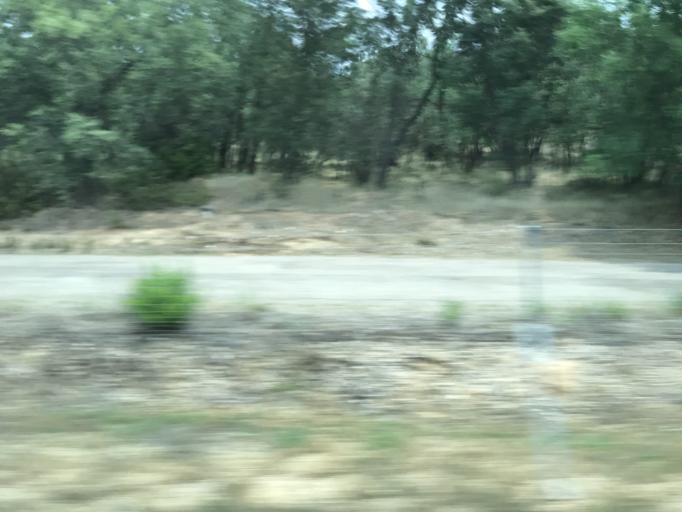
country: ES
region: Castille and Leon
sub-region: Provincia de Burgos
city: Aranda de Duero
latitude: 41.7043
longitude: -3.7000
